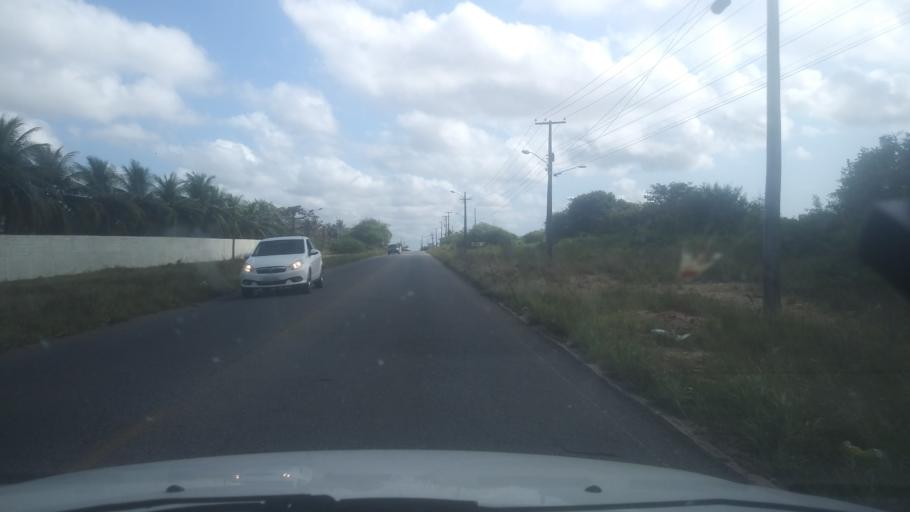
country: BR
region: Rio Grande do Norte
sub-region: Extremoz
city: Extremoz
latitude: -5.7170
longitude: -35.2774
